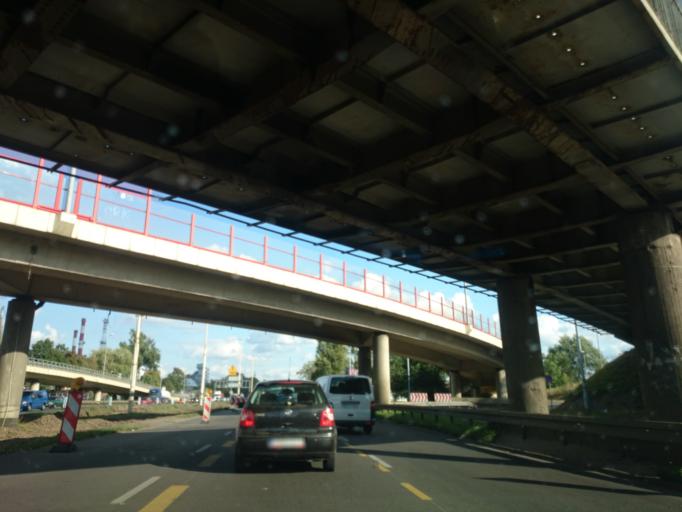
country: PL
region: West Pomeranian Voivodeship
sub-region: Szczecin
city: Szczecin
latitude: 53.4134
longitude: 14.5746
